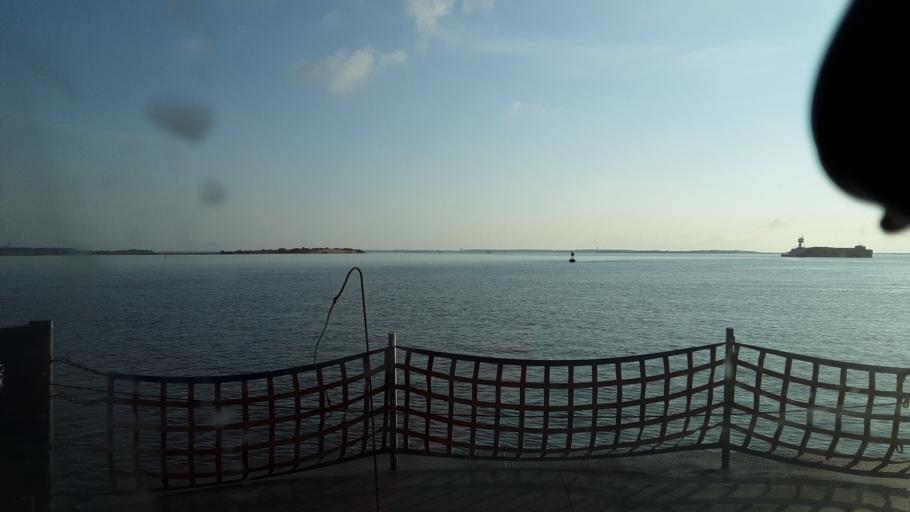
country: US
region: North Carolina
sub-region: Brunswick County
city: Southport
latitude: 33.9449
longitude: -77.9719
